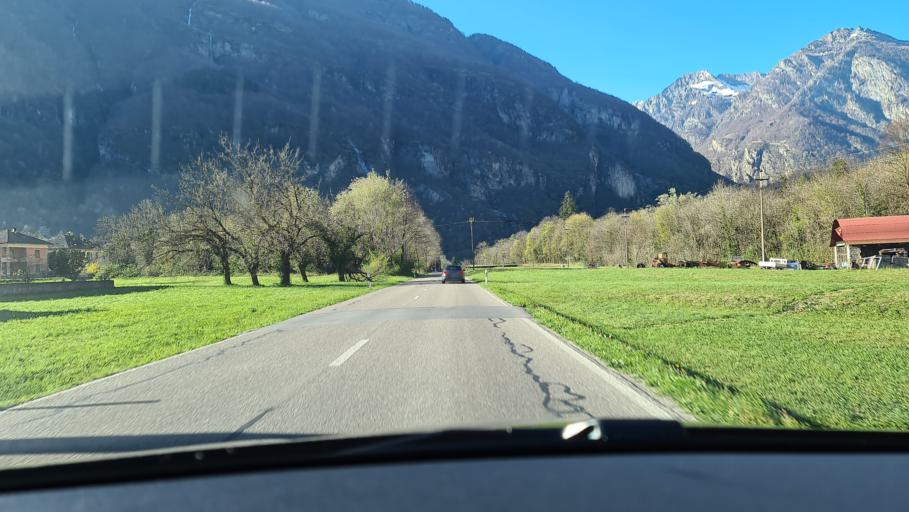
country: CH
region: Ticino
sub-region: Vallemaggia District
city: Cevio
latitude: 46.3116
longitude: 8.6065
